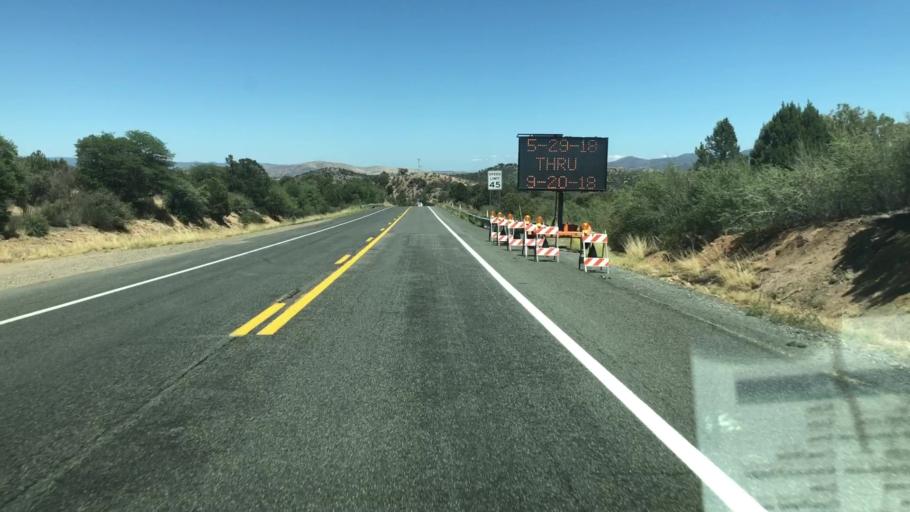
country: US
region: Arizona
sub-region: Yavapai County
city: Prescott
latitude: 34.5813
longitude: -112.5366
